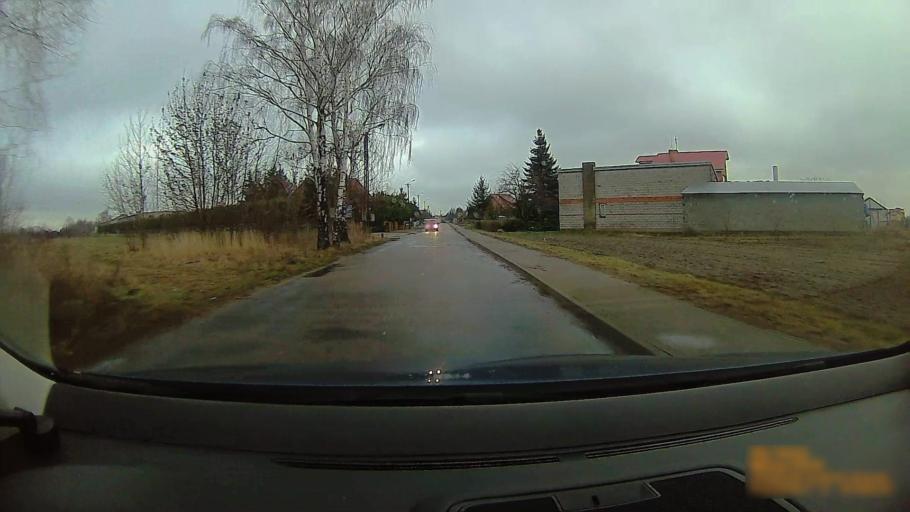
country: PL
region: Greater Poland Voivodeship
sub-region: Powiat koninski
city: Rychwal
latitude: 52.0746
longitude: 18.1523
